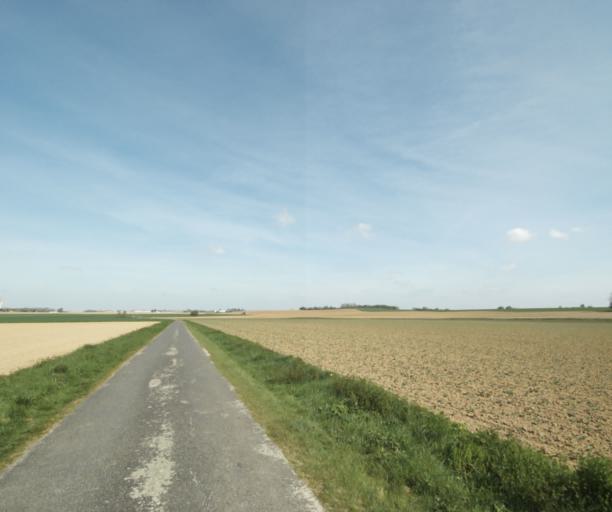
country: FR
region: Ile-de-France
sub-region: Departement de Seine-et-Marne
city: Nangis
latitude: 48.5419
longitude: 3.0369
